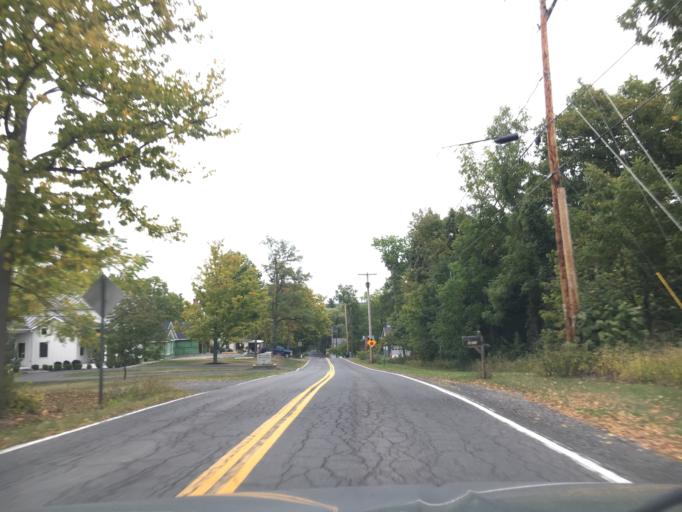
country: US
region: New York
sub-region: Tompkins County
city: Trumansburg
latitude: 42.6639
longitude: -76.7042
